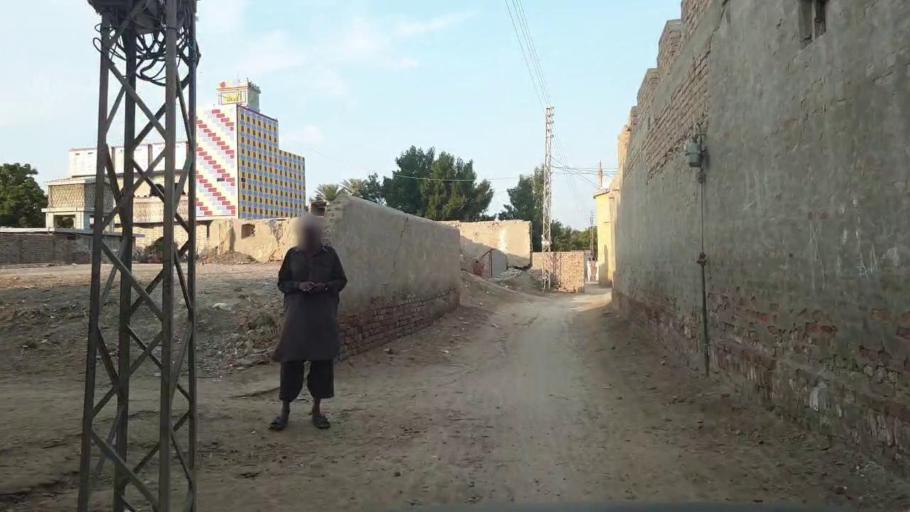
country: PK
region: Sindh
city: Shahpur Chakar
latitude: 26.1636
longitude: 68.6266
